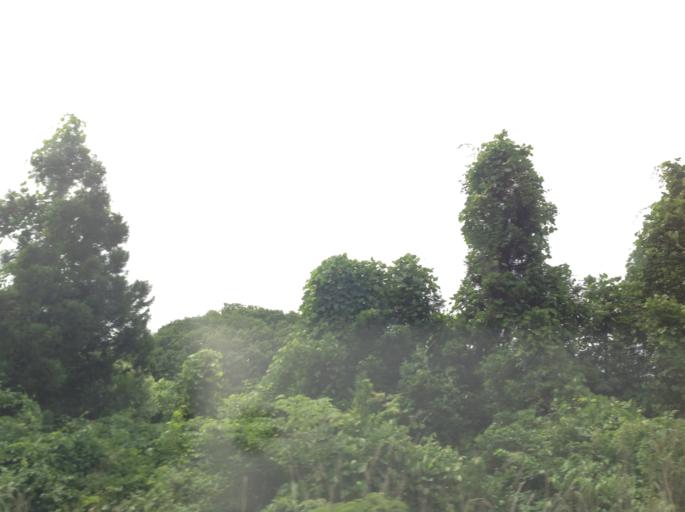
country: JP
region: Miyagi
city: Sendai-shi
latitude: 38.3179
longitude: 140.8279
